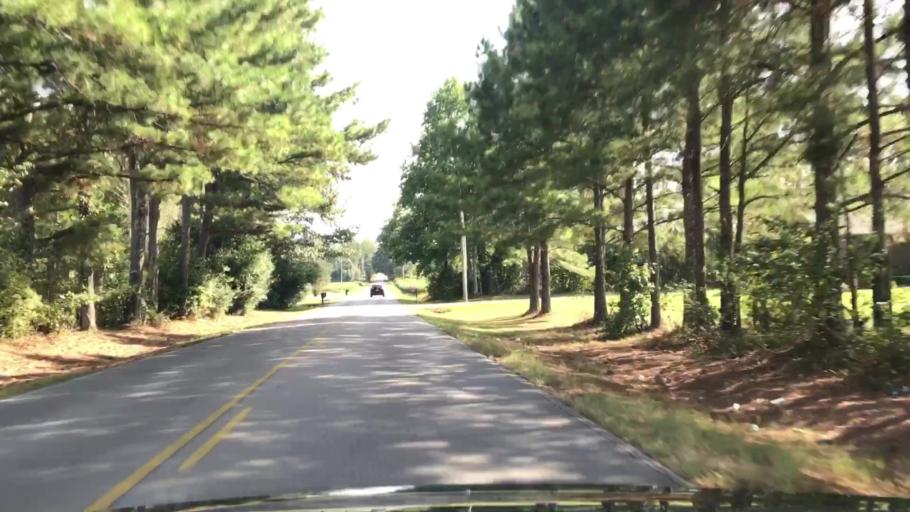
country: US
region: Alabama
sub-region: Madison County
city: Harvest
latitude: 34.8899
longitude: -86.7487
